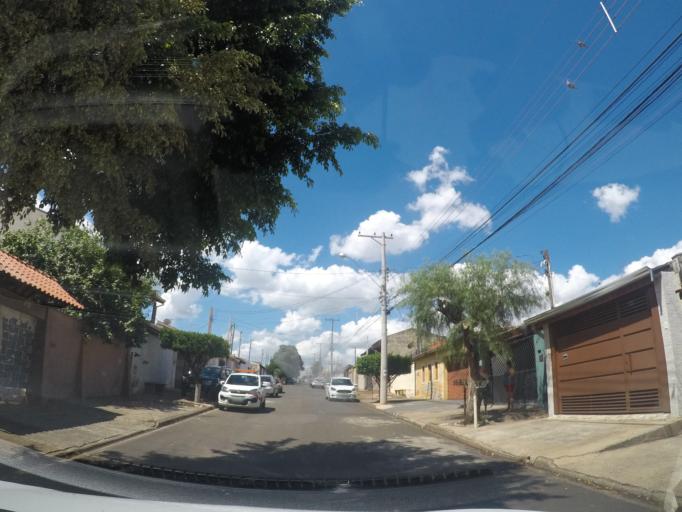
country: BR
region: Sao Paulo
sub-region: Sumare
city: Sumare
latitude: -22.8353
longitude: -47.2758
